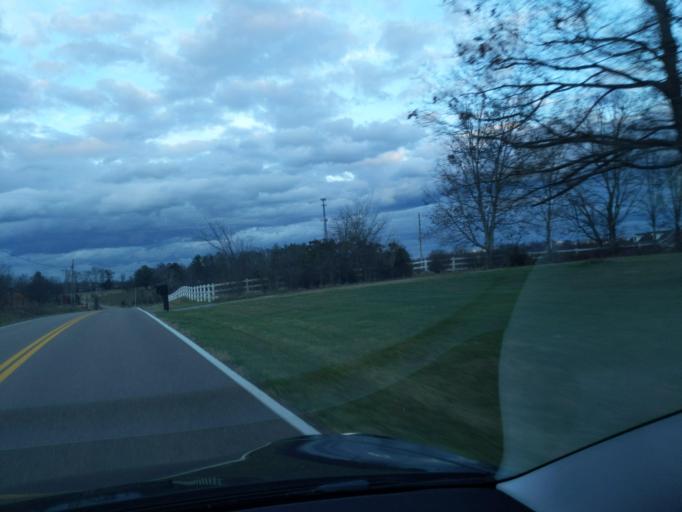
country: US
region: Tennessee
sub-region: Jefferson County
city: Dandridge
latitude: 36.0851
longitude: -83.3688
